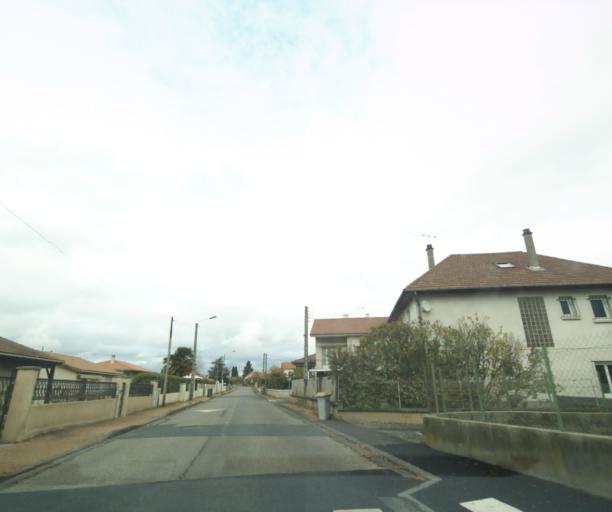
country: FR
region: Auvergne
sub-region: Departement du Puy-de-Dome
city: Pont-du-Chateau
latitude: 45.8043
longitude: 3.2443
